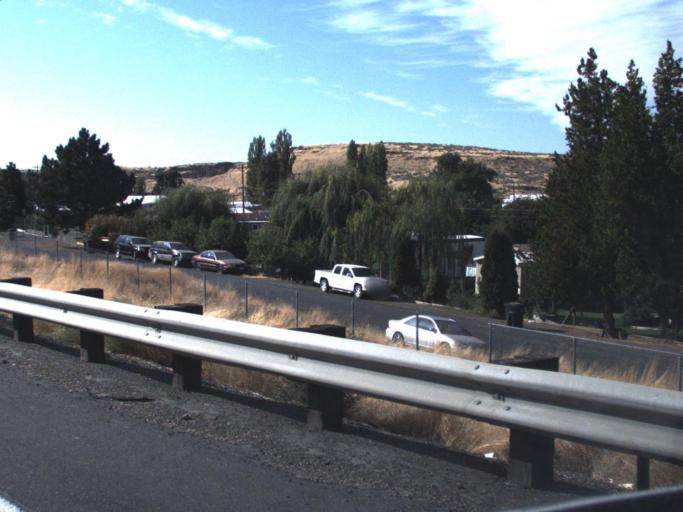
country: US
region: Washington
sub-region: Franklin County
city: Basin City
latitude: 46.5797
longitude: -119.0041
